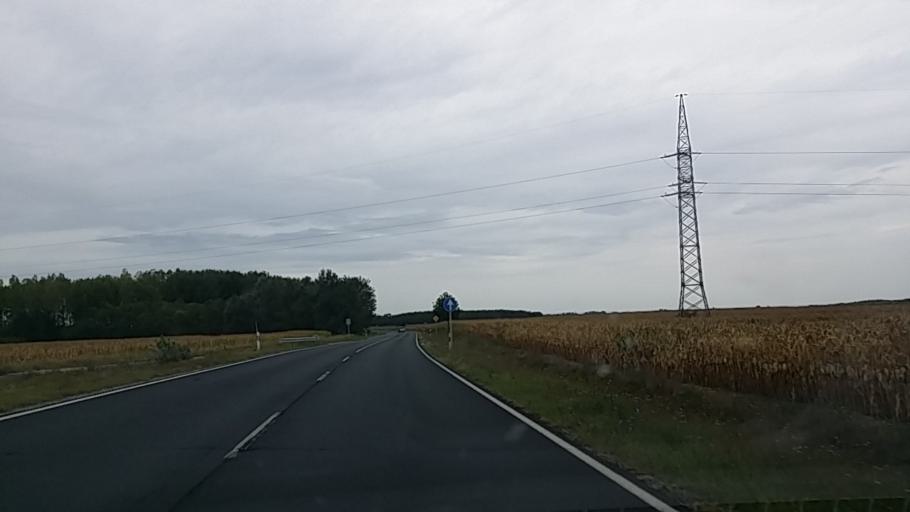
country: HU
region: Gyor-Moson-Sopron
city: Fertoszentmiklos
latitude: 47.5933
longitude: 16.9385
